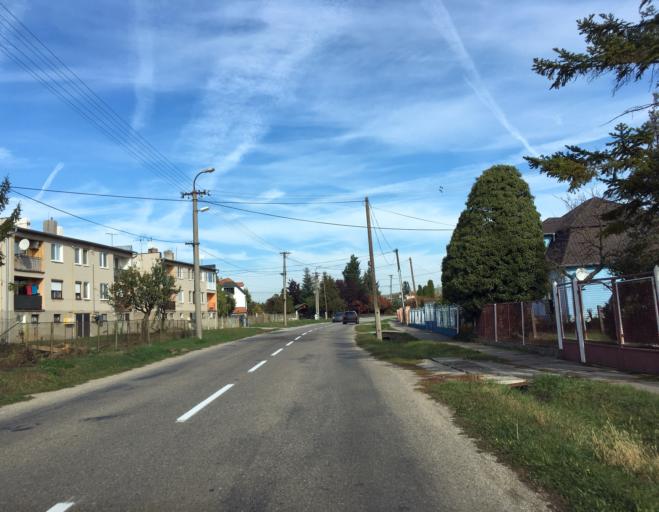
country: SK
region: Nitriansky
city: Svodin
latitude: 48.0120
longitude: 18.4135
